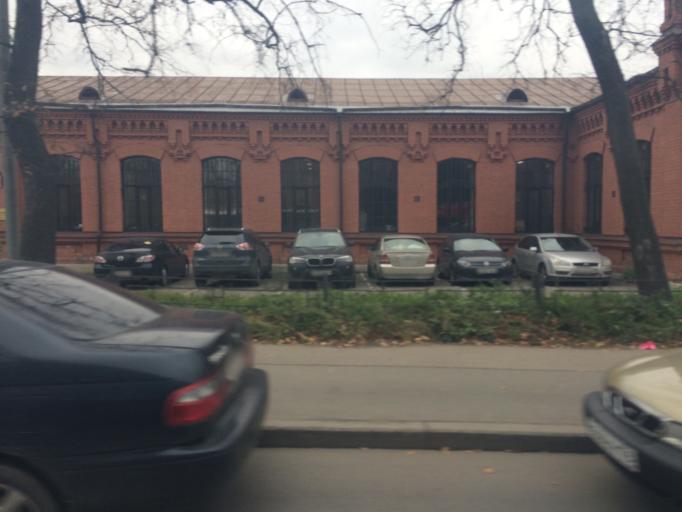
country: RU
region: Leningrad
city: Rybatskoye
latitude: 59.8597
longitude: 30.4791
